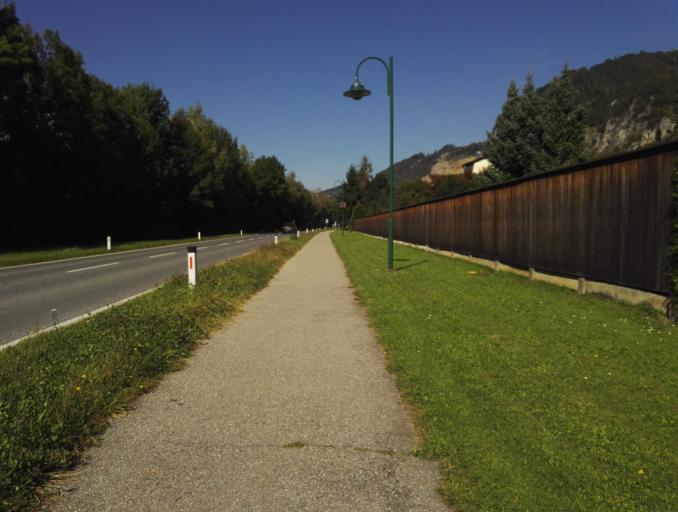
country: AT
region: Styria
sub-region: Politischer Bezirk Graz-Umgebung
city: Peggau
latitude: 47.1969
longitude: 15.3461
